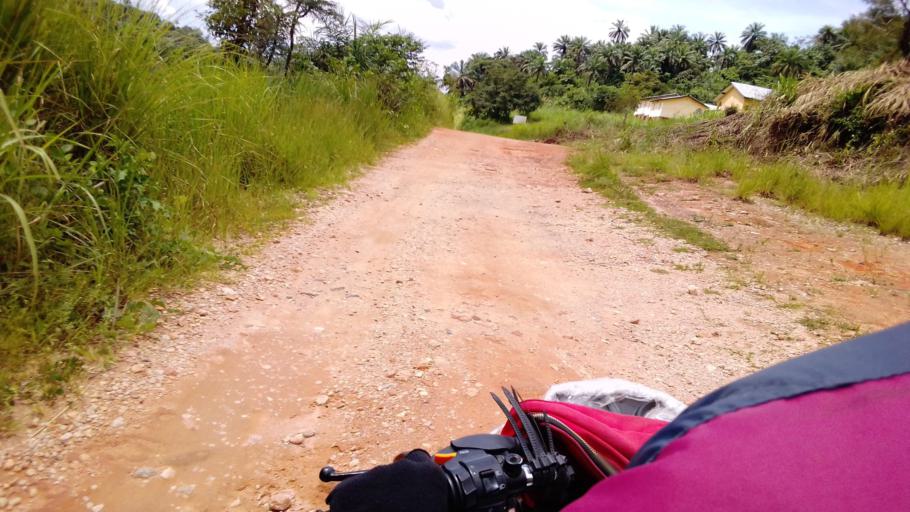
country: SL
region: Eastern Province
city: Koyima
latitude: 8.6904
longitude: -11.0085
